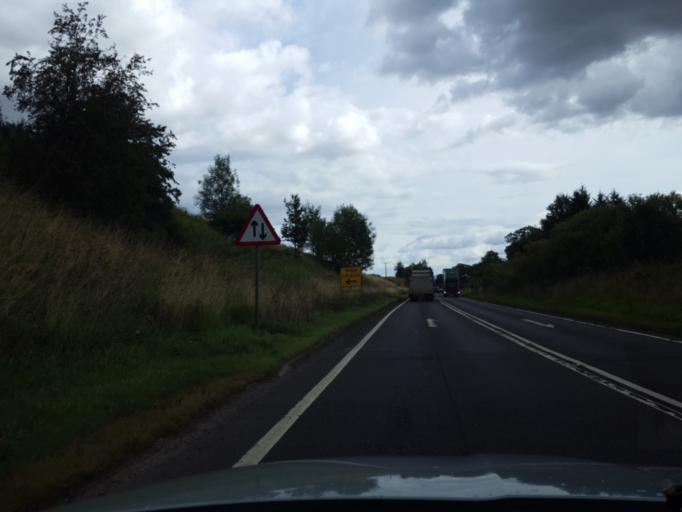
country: GB
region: Scotland
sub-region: Perth and Kinross
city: Bankfoot
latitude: 56.4882
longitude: -3.5018
